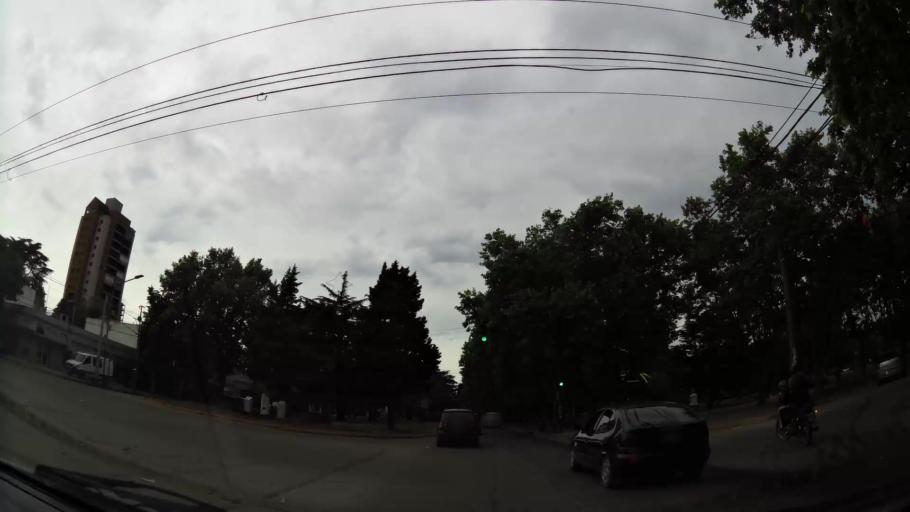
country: AR
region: Buenos Aires
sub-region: Partido de Quilmes
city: Quilmes
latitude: -34.8038
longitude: -58.2785
